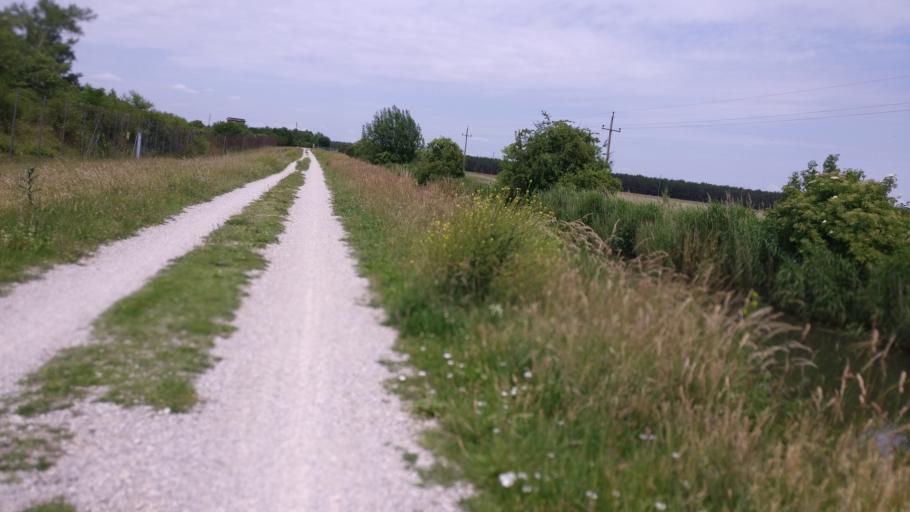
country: AT
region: Lower Austria
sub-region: Politischer Bezirk Wiener Neustadt
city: Lichtenworth
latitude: 47.8540
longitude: 16.2795
